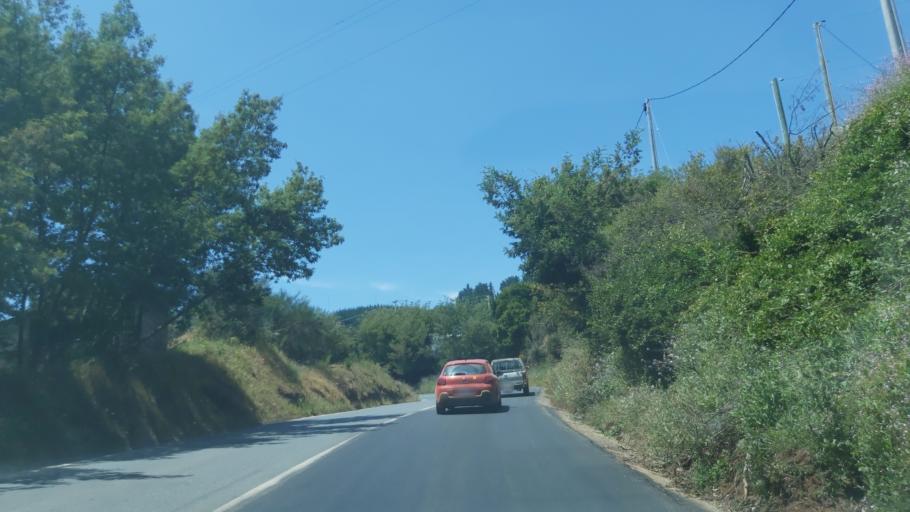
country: CL
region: Maule
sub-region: Provincia de Cauquenes
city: Cauquenes
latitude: -35.8257
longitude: -72.6080
